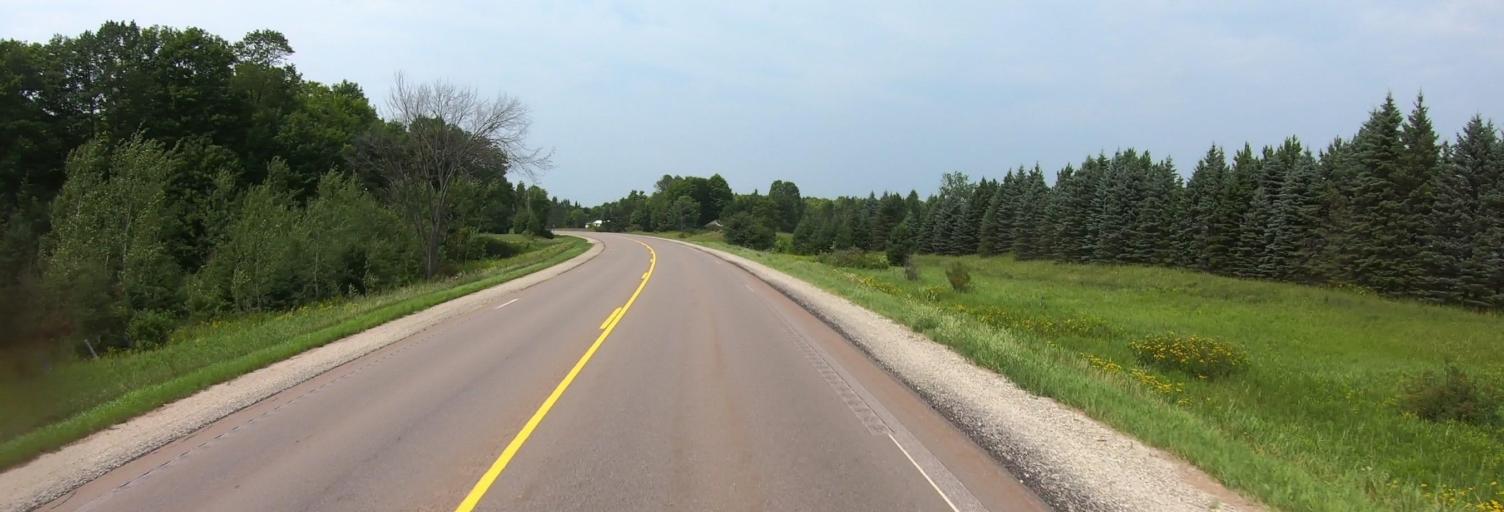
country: US
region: Michigan
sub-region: Alger County
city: Munising
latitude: 46.3495
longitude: -86.9532
